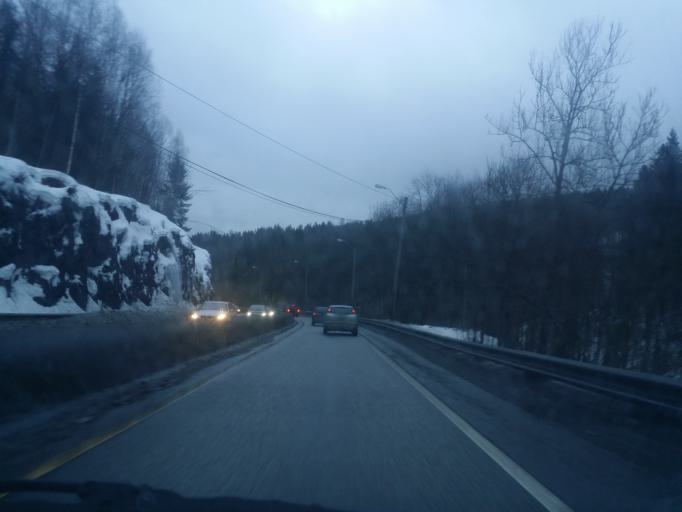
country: NO
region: Akershus
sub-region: Baerum
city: Skui
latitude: 59.9390
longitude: 10.4092
